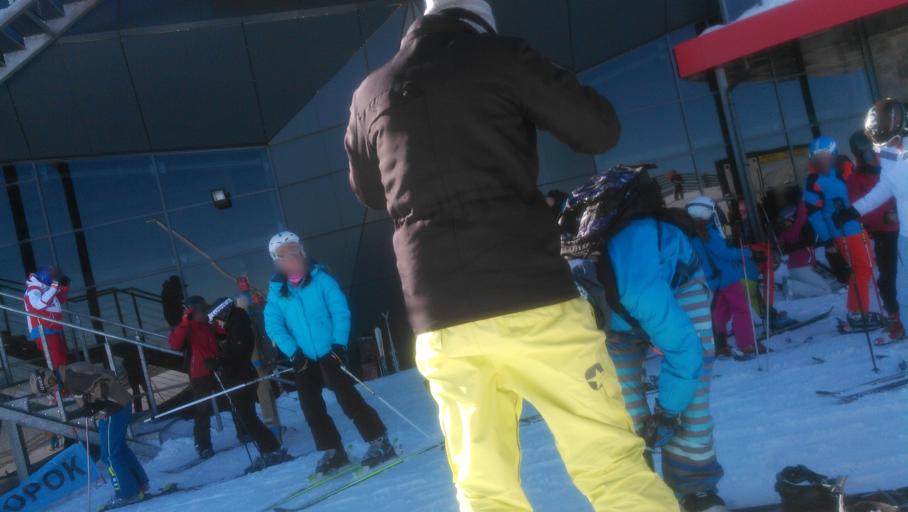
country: SK
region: Zilinsky
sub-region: Okres Liptovsky Mikulas
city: Liptovsky Mikulas
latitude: 48.9437
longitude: 19.5904
